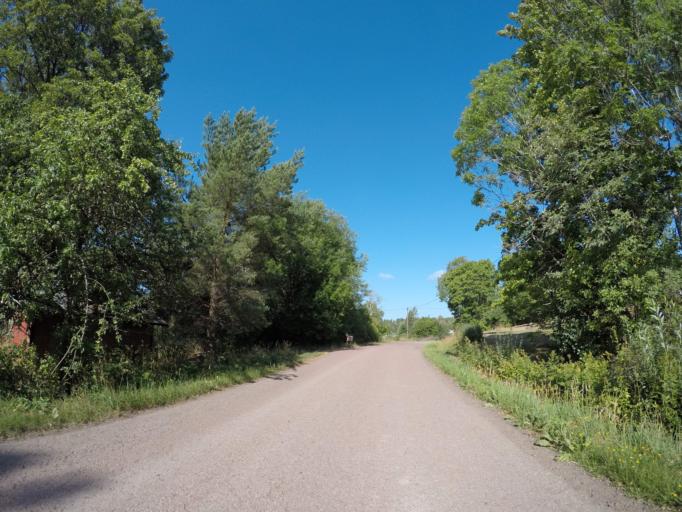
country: AX
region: Alands landsbygd
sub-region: Finstroem
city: Finstroem
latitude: 60.2489
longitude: 19.9216
